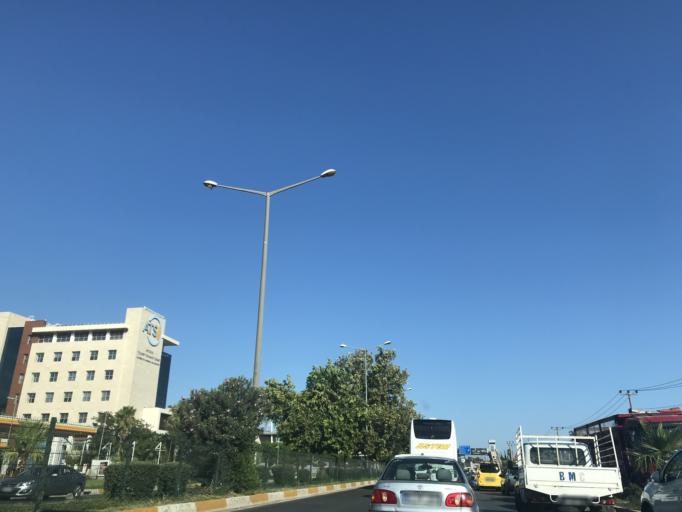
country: TR
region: Antalya
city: Antalya
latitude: 36.9024
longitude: 30.7579
